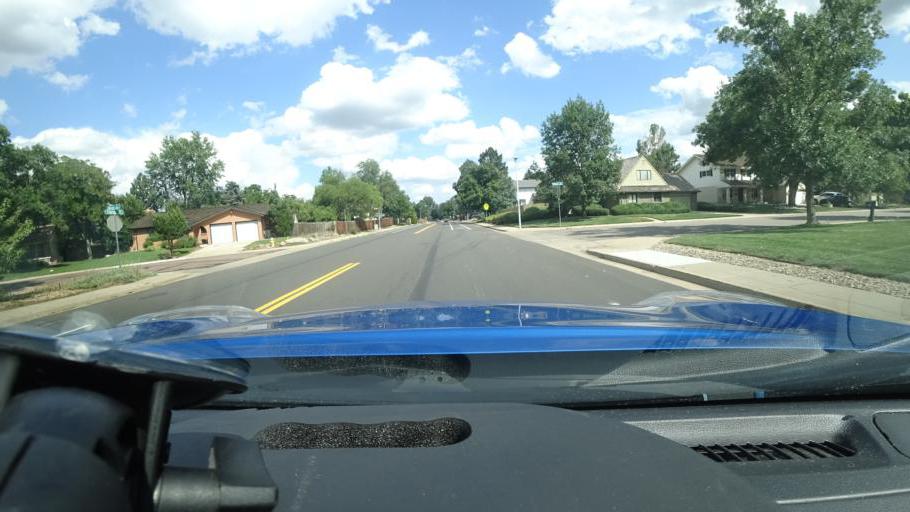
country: US
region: Colorado
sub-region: Adams County
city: Aurora
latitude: 39.6893
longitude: -104.8562
